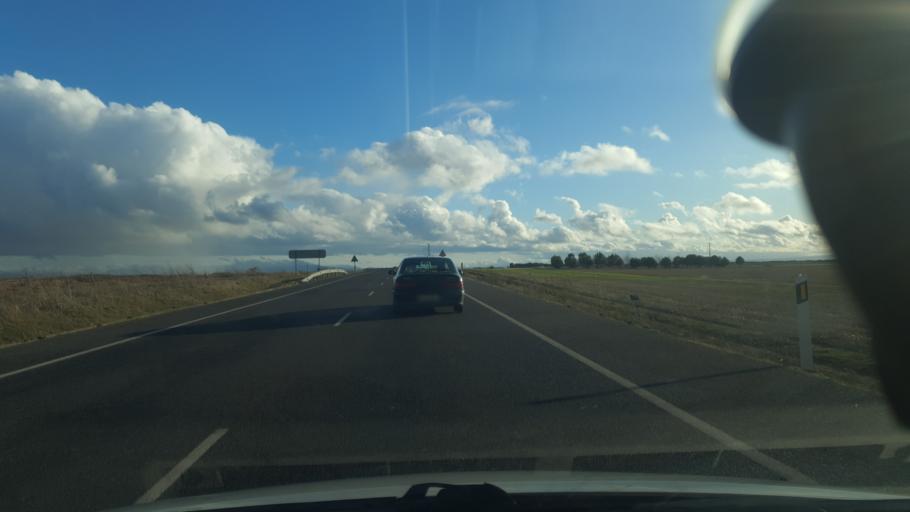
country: ES
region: Castille and Leon
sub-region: Provincia de Segovia
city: Rapariegos
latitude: 41.0890
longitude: -4.6372
